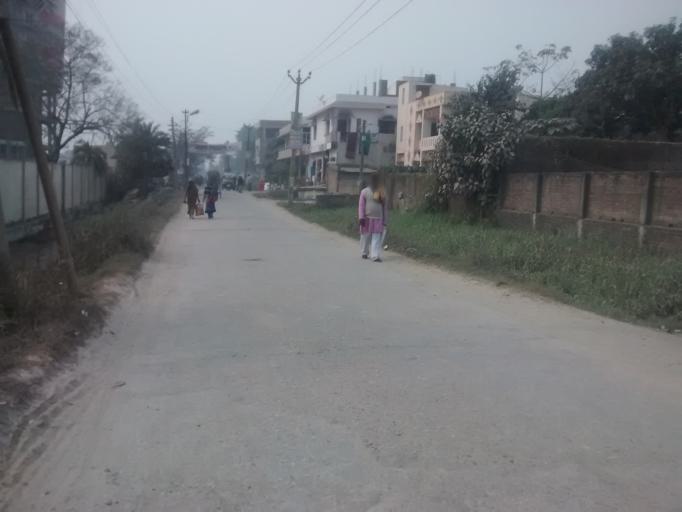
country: IN
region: Bihar
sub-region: Muzaffarpur
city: Muzaffarpur
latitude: 26.1020
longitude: 85.4104
